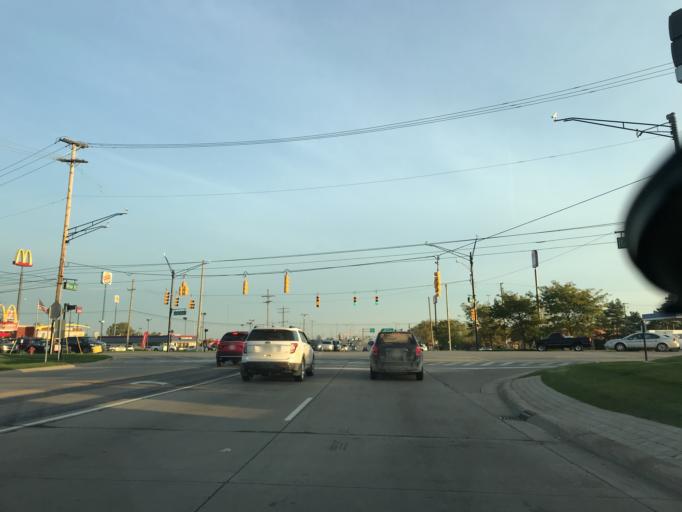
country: US
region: Michigan
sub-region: Oakland County
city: Wixom
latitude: 42.4937
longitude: -83.5358
